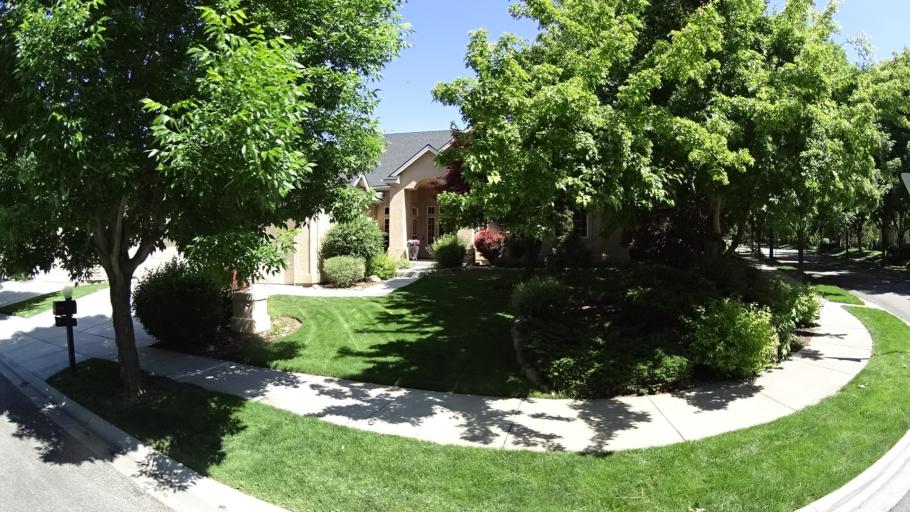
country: US
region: Idaho
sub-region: Ada County
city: Boise
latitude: 43.5707
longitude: -116.1183
